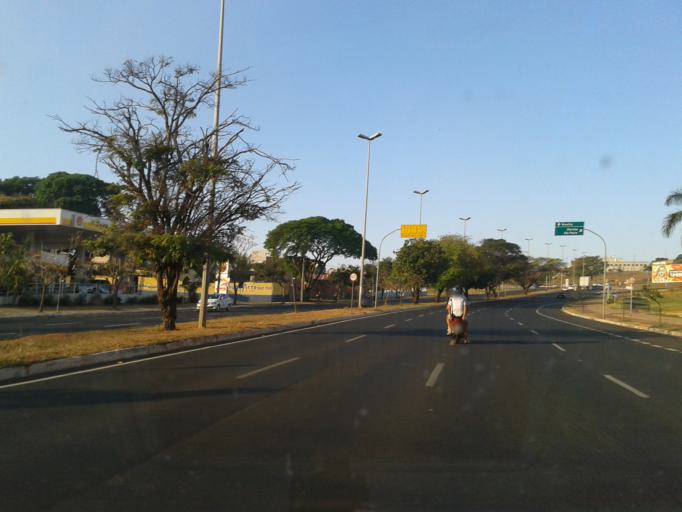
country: BR
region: Minas Gerais
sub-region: Uberlandia
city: Uberlandia
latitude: -18.8961
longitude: -48.2547
